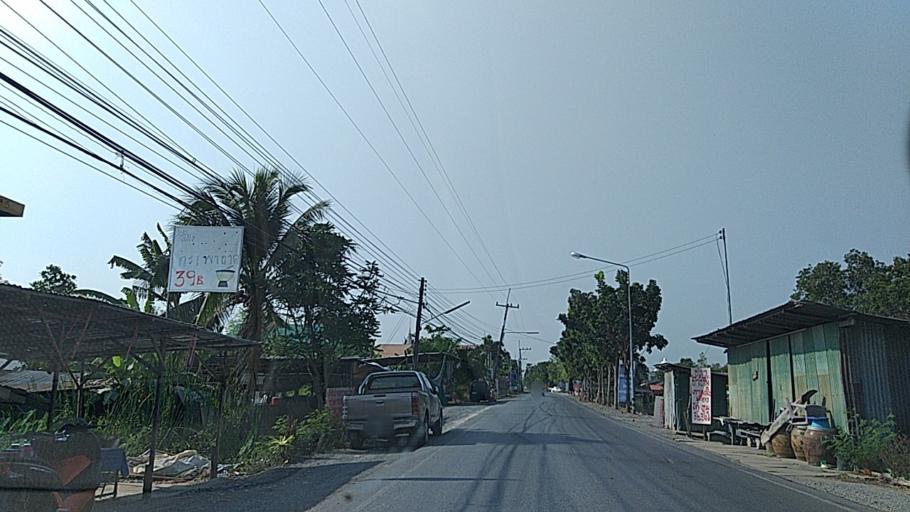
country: TH
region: Pathum Thani
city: Lam Luk Ka
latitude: 13.9535
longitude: 100.7058
